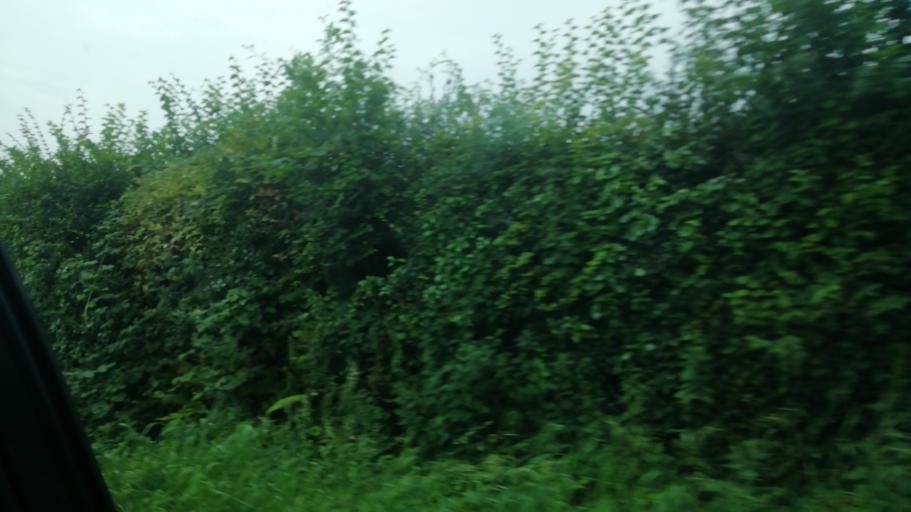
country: IE
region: Leinster
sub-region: Kilkenny
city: Callan
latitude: 52.5457
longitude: -7.5285
